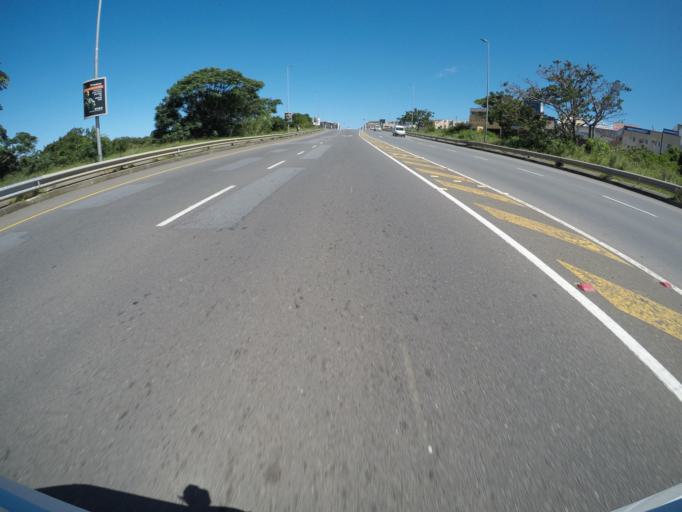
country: ZA
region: Eastern Cape
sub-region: Buffalo City Metropolitan Municipality
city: East London
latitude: -33.0055
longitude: 27.9130
